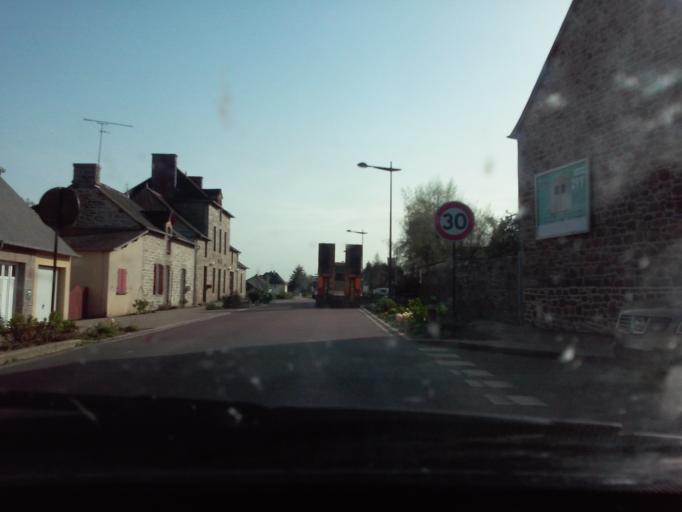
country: FR
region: Brittany
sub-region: Departement d'Ille-et-Vilaine
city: Saint-Jean-sur-Couesnon
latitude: 48.2903
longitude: -1.3694
